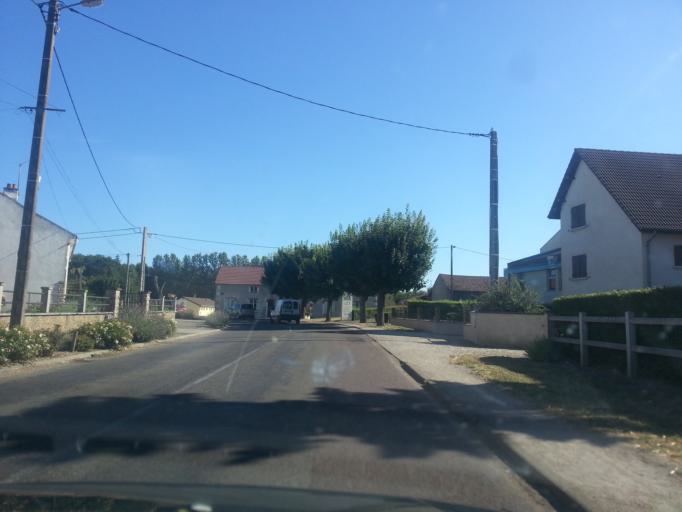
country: FR
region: Bourgogne
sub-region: Departement de Saone-et-Loire
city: Verdun-sur-le-Doubs
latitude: 46.8931
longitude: 5.0234
